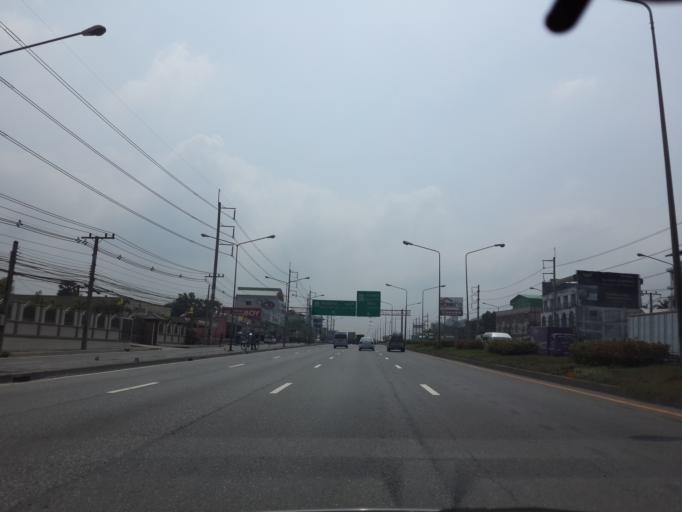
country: TH
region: Chon Buri
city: Chon Buri
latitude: 13.3933
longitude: 101.0107
